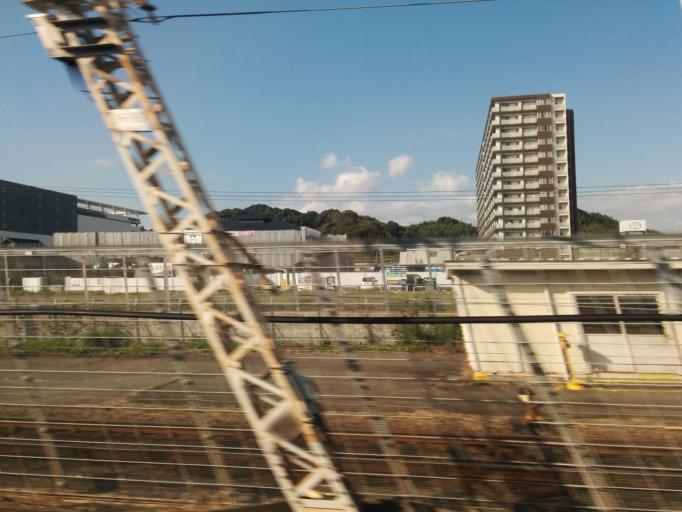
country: JP
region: Shizuoka
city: Shizuoka-shi
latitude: 34.9844
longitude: 138.4128
